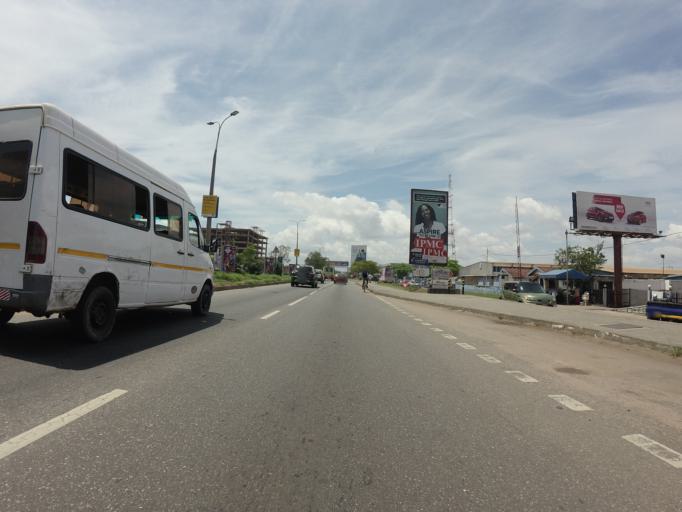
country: GH
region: Greater Accra
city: Accra
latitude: 5.5586
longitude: -0.2246
